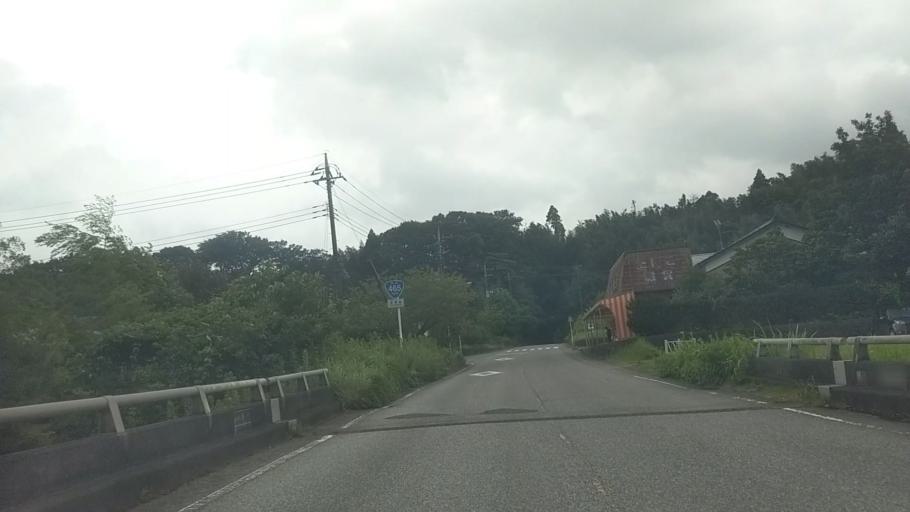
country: JP
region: Chiba
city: Kimitsu
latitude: 35.2516
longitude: 139.9958
